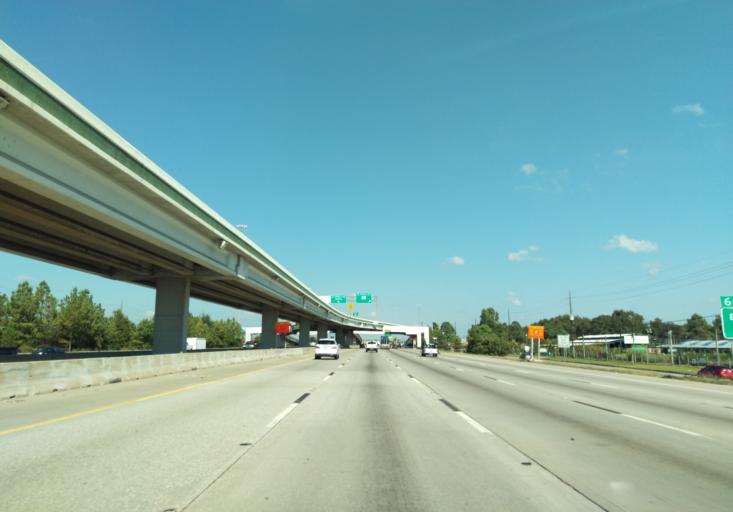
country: US
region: Texas
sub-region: Harris County
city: Spring
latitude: 30.0105
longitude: -95.4277
